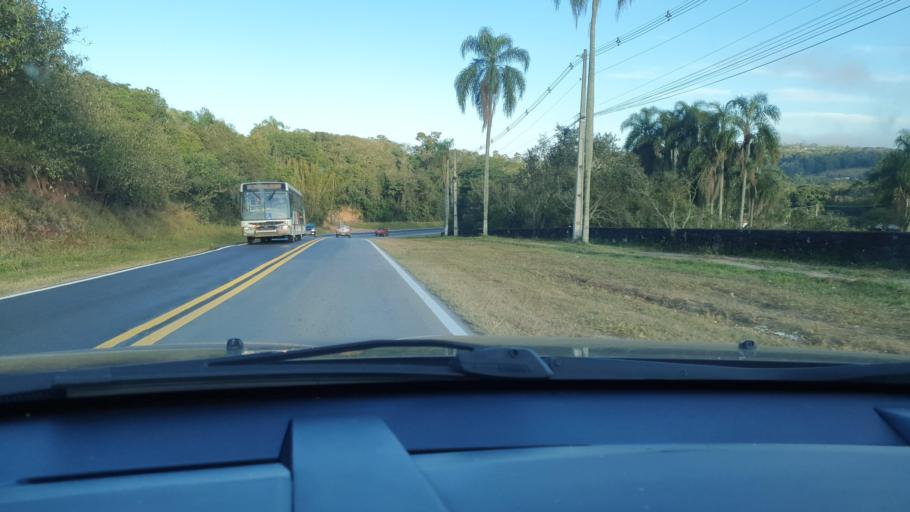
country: BR
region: Sao Paulo
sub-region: Ibiuna
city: Ibiuna
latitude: -23.6763
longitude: -47.3057
